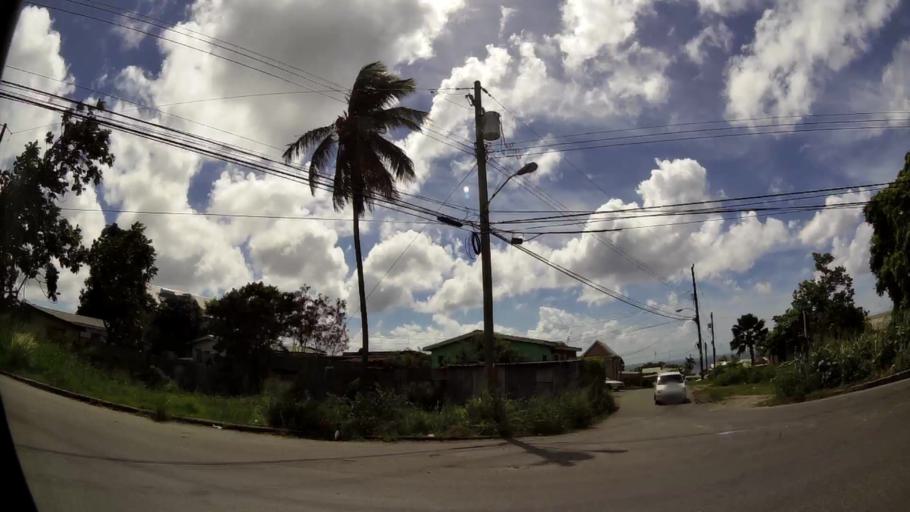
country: BB
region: Saint Michael
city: Bridgetown
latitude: 13.1346
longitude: -59.6225
